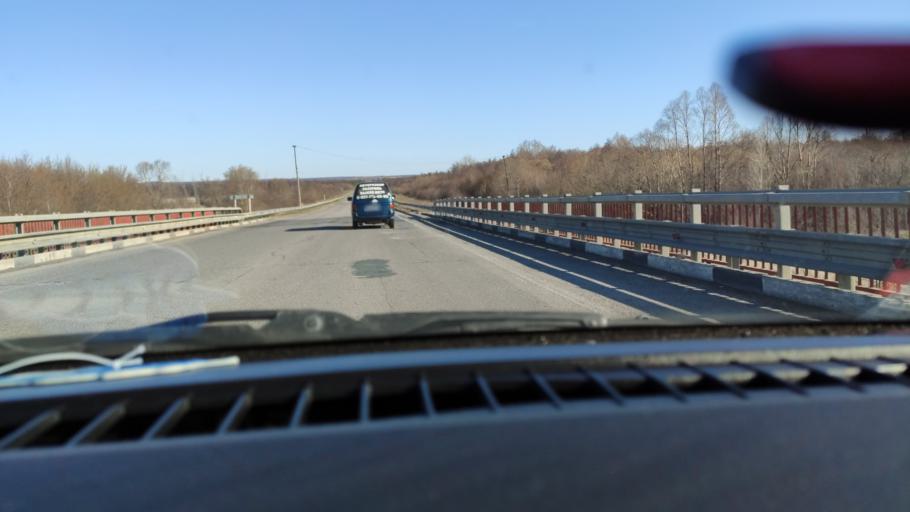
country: RU
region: Samara
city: Varlamovo
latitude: 53.1335
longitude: 48.2870
